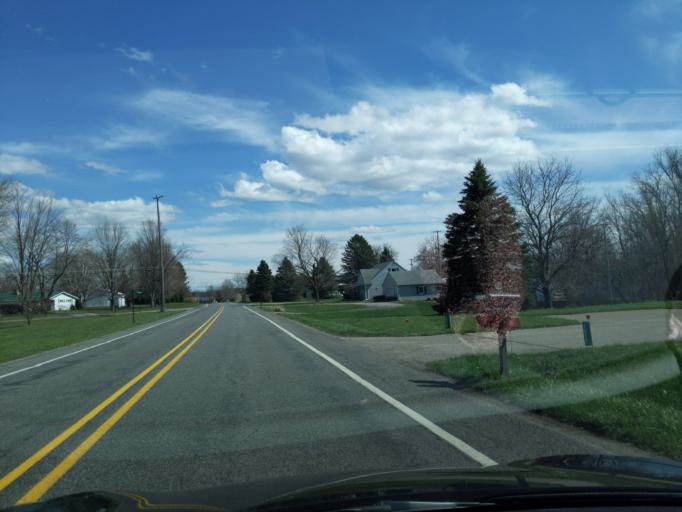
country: US
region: Michigan
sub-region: Ingham County
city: Mason
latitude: 42.5577
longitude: -84.4047
